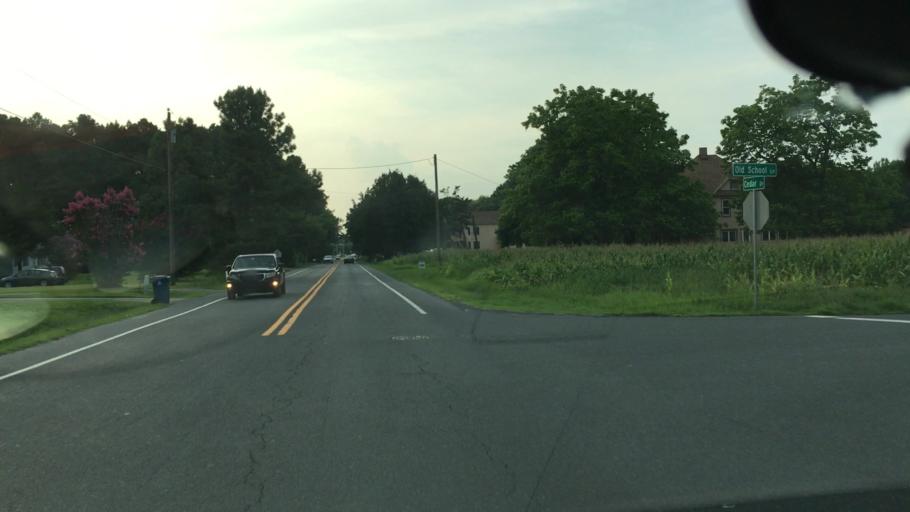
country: US
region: Delaware
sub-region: Sussex County
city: Ocean View
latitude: 38.5434
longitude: -75.1023
